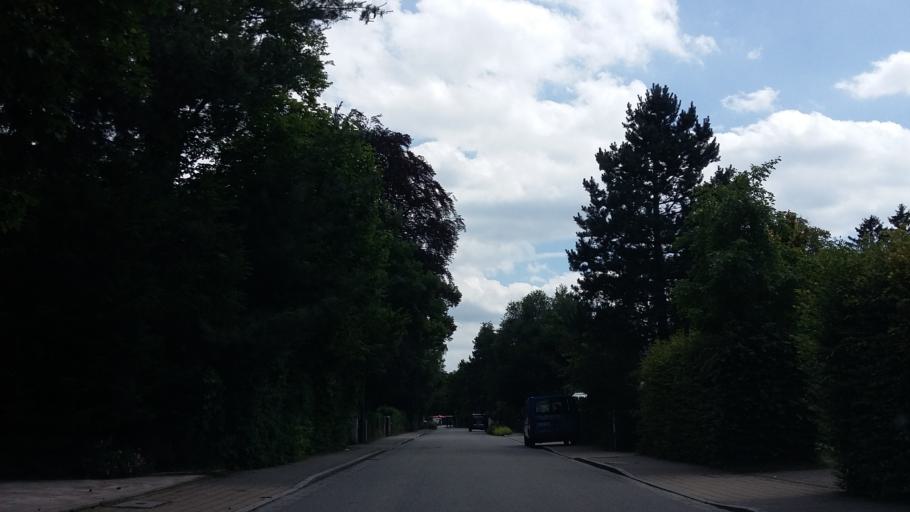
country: DE
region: Bavaria
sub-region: Upper Bavaria
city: Grafelfing
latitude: 48.1324
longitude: 11.4305
